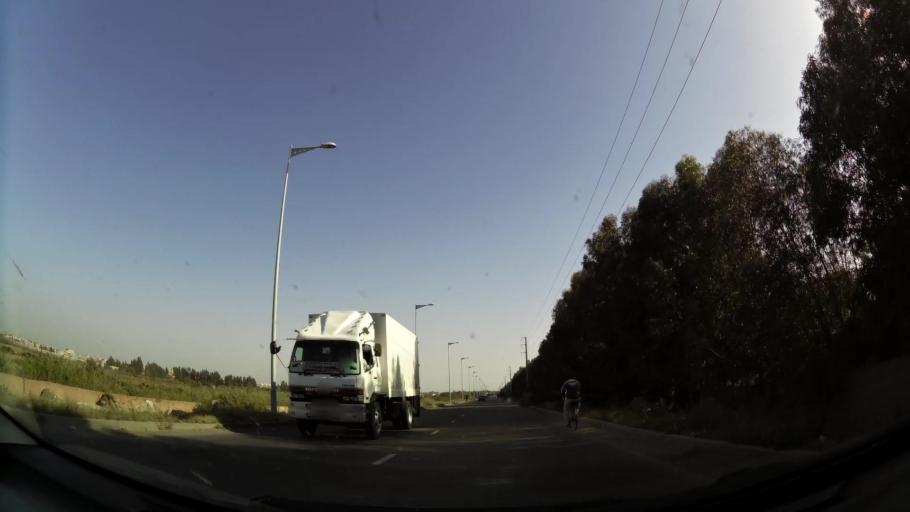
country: MA
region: Souss-Massa-Draa
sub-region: Inezgane-Ait Mellou
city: Inezgane
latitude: 30.3584
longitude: -9.5059
